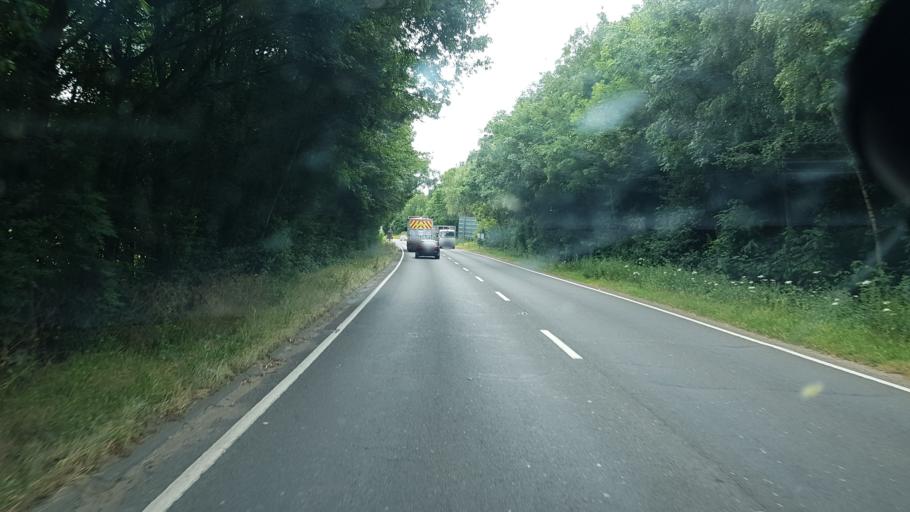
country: GB
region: England
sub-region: Surrey
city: Godstone
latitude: 51.2486
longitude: -0.0527
